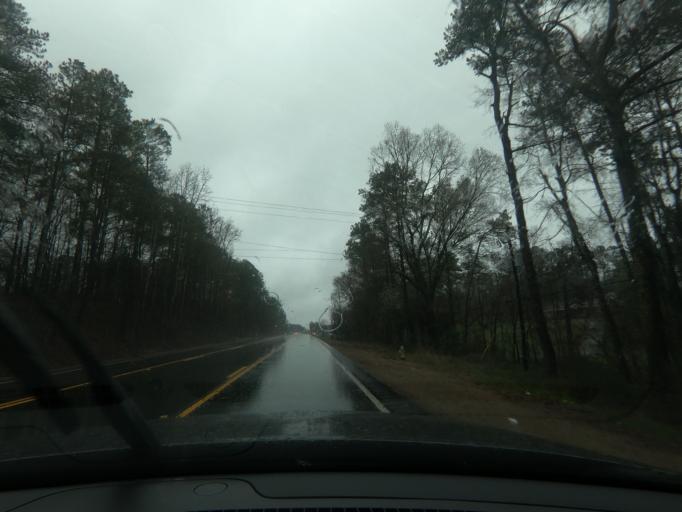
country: US
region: Georgia
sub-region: Bartow County
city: Adairsville
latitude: 34.3533
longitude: -84.9185
